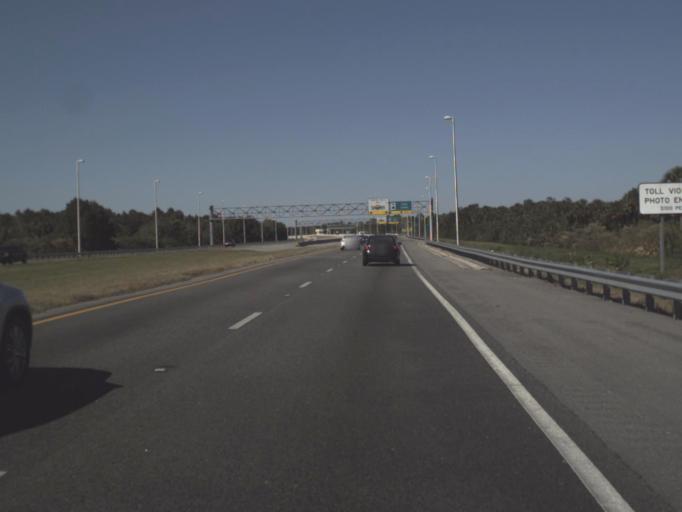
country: US
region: Florida
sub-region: Seminole County
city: Midway
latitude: 28.7328
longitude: -81.2510
